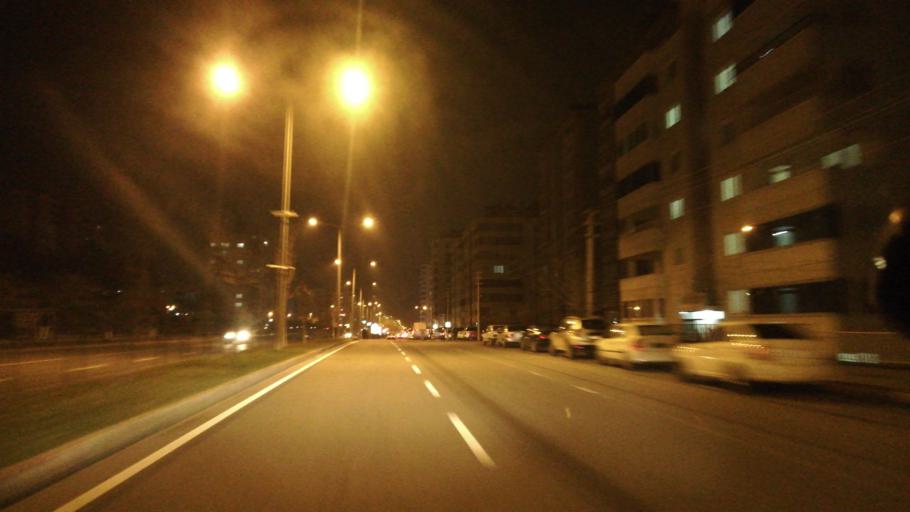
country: TR
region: Kahramanmaras
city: Kahramanmaras
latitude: 37.5964
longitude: 36.8801
